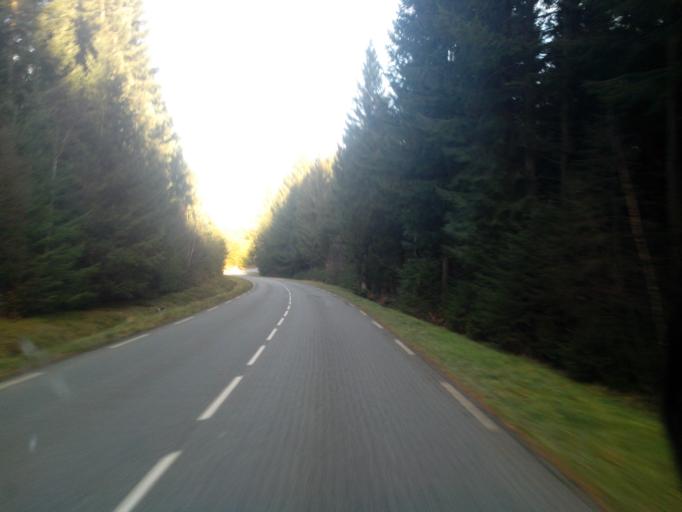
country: FR
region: Limousin
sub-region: Departement de la Correze
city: Meymac
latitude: 45.5745
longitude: 2.0915
